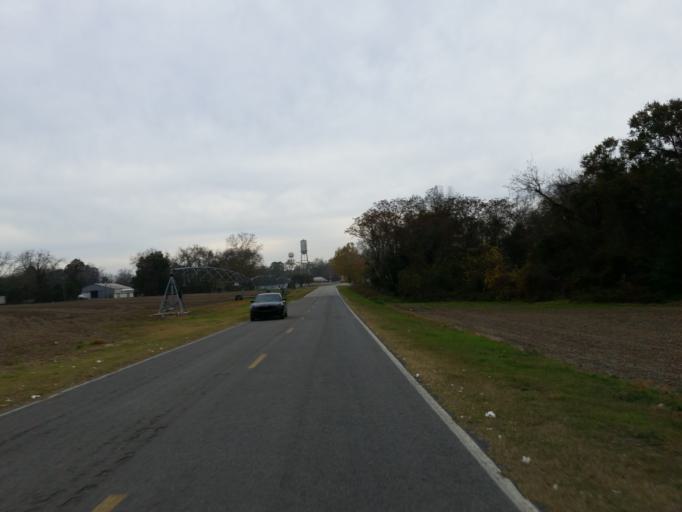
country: US
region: Georgia
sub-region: Dooly County
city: Unadilla
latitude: 32.1939
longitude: -83.7557
